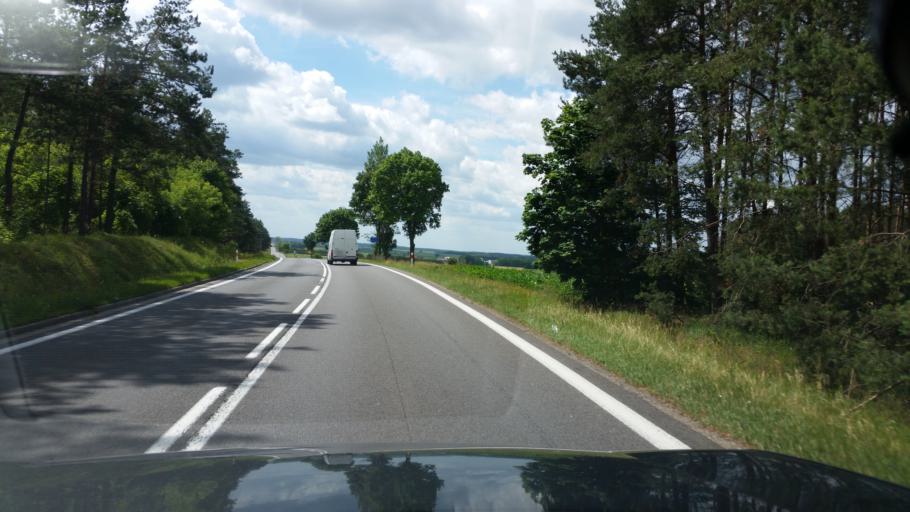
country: PL
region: Podlasie
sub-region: Powiat kolnenski
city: Stawiski
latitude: 53.4364
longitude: 22.1739
